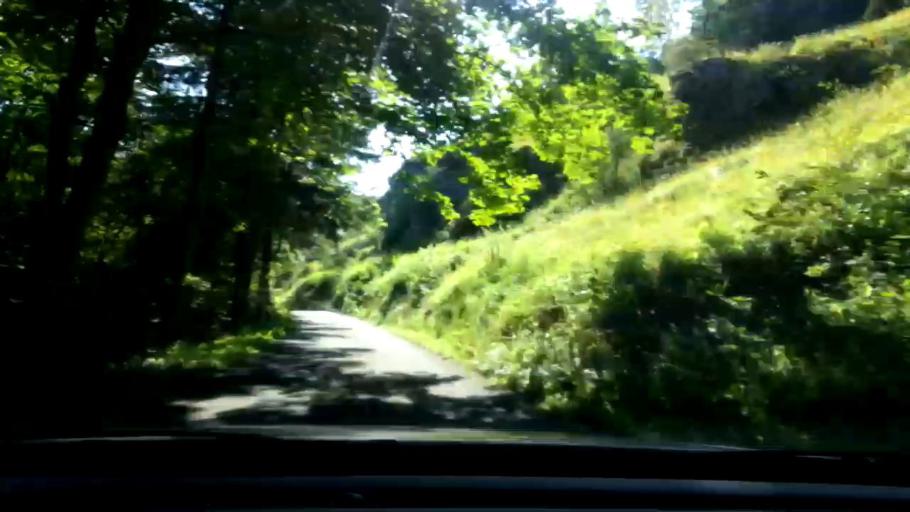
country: DE
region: Bavaria
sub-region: Upper Franconia
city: Wattendorf
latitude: 50.0053
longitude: 11.1008
